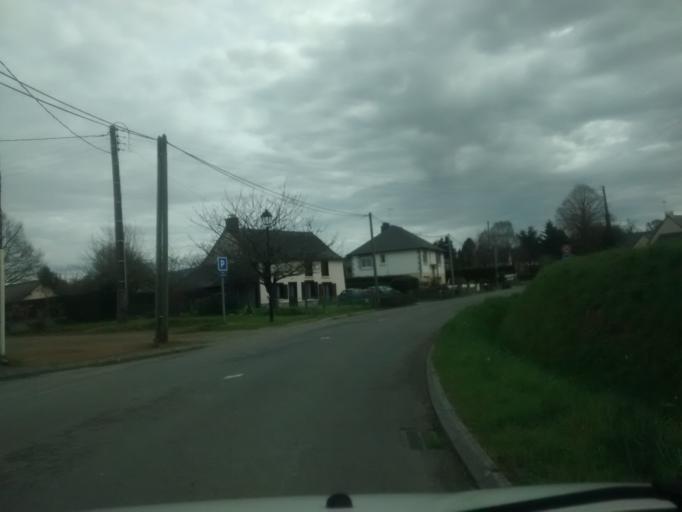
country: FR
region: Brittany
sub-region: Departement d'Ille-et-Vilaine
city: Saint-Sulpice-la-Foret
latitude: 48.2229
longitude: -1.5786
